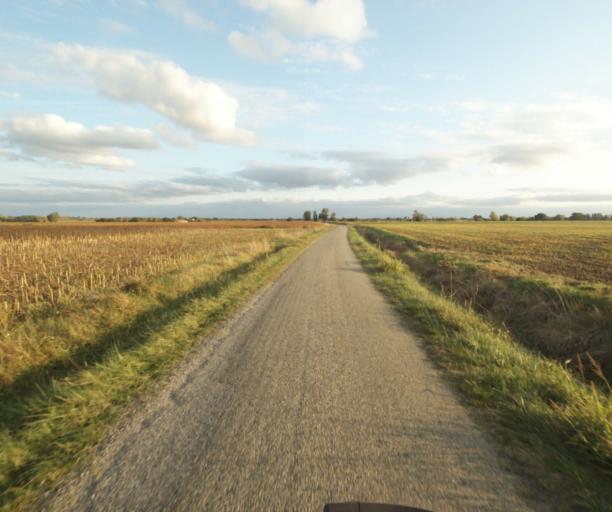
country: FR
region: Midi-Pyrenees
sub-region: Departement de la Haute-Garonne
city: Launac
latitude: 43.8177
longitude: 1.1614
